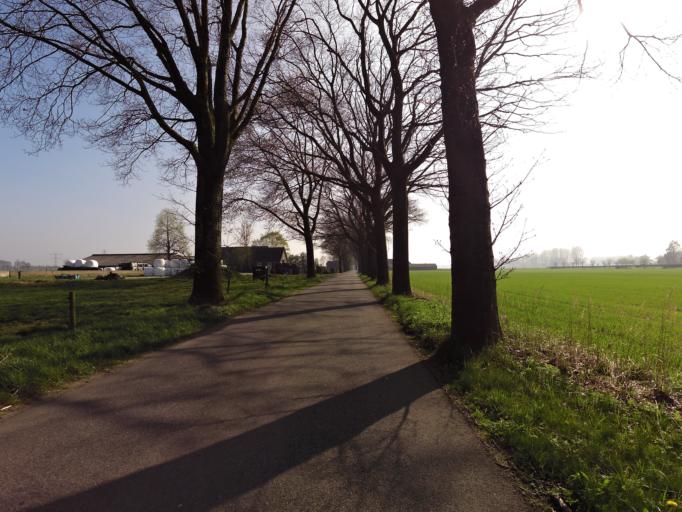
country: NL
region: Gelderland
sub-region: Gemeente Bronckhorst
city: Baak
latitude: 52.0482
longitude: 6.2481
